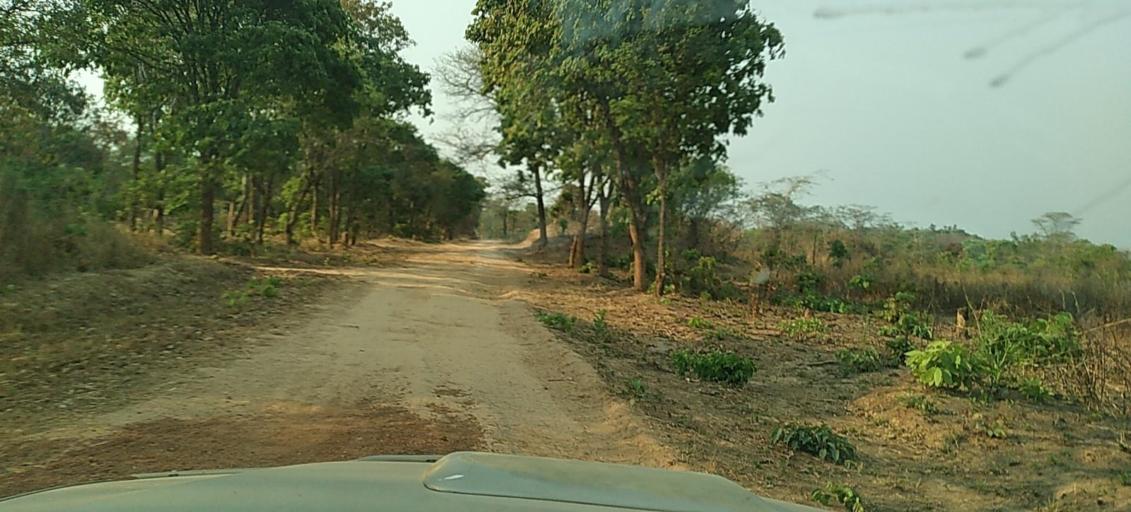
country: ZM
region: North-Western
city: Kasempa
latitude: -13.2801
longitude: 26.5551
